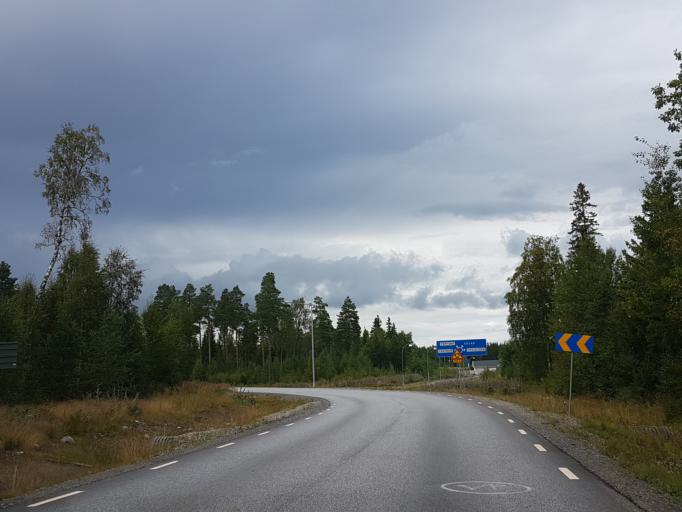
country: SE
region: Vaesterbotten
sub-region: Umea Kommun
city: Holmsund
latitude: 63.8008
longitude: 20.3649
